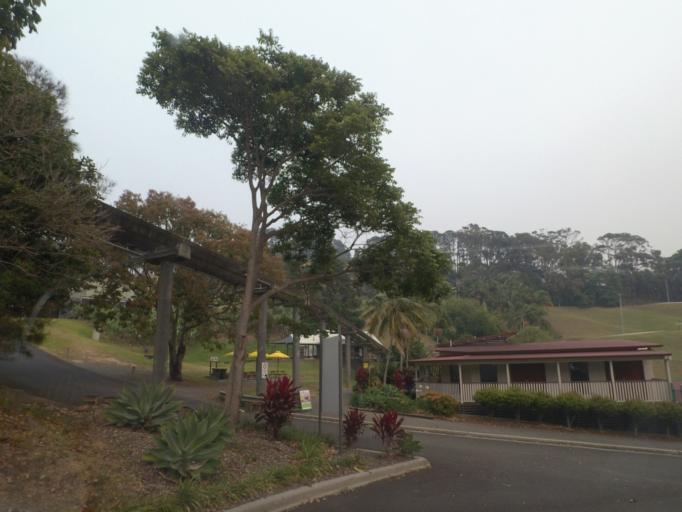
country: AU
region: New South Wales
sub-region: Coffs Harbour
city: Coffs Harbour
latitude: -30.2745
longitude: 153.1312
